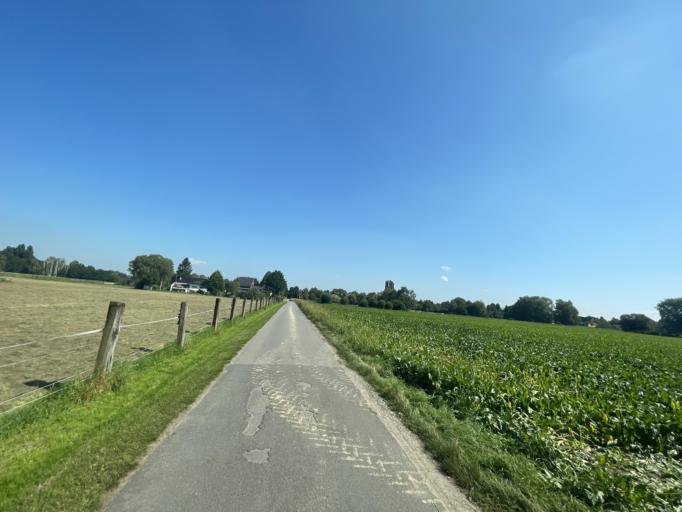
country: DE
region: North Rhine-Westphalia
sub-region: Regierungsbezirk Dusseldorf
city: Krefeld
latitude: 51.3688
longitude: 6.5609
